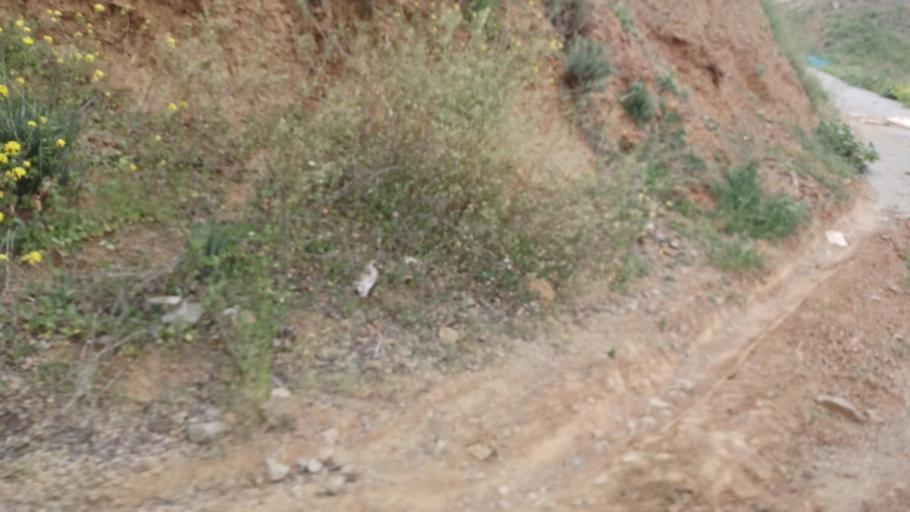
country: CY
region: Limassol
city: Pelendri
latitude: 34.8637
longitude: 33.0850
